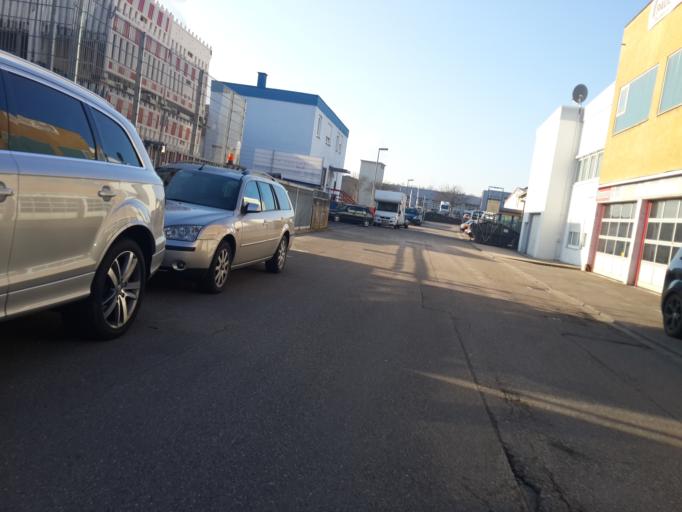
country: DE
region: Baden-Wuerttemberg
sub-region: Regierungsbezirk Stuttgart
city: Untereisesheim
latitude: 49.1907
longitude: 9.2028
